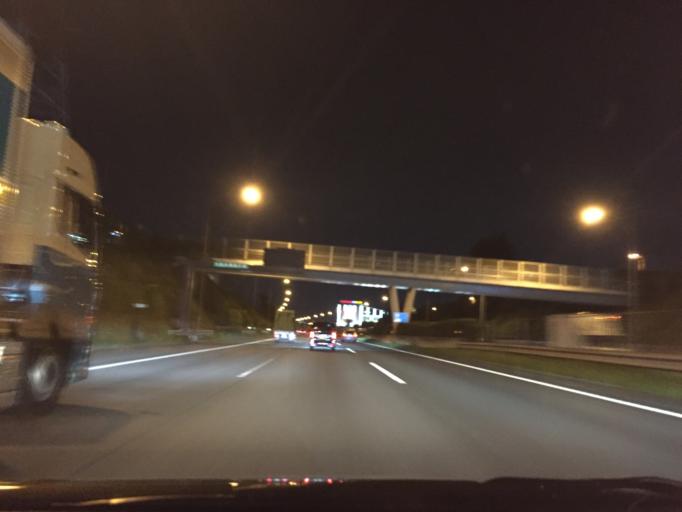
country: JP
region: Kanagawa
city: Minami-rinkan
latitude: 35.4976
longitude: 139.4747
